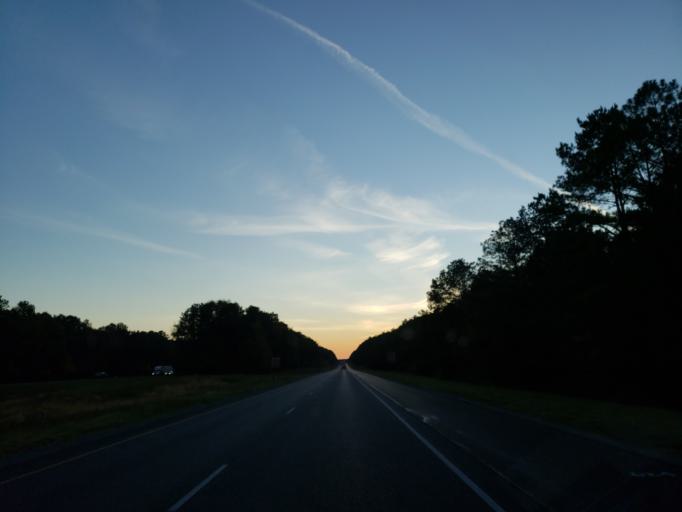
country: US
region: Alabama
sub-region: Sumter County
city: Livingston
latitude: 32.5805
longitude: -88.2356
